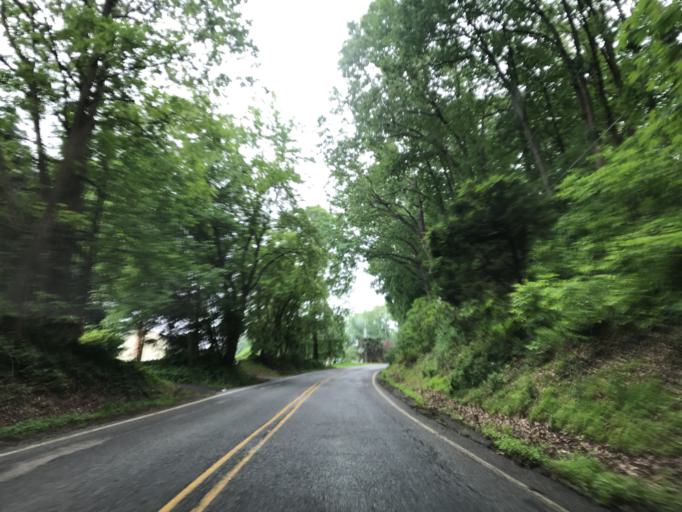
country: US
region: Pennsylvania
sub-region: York County
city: Susquehanna Trails
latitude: 39.7584
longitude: -76.4625
